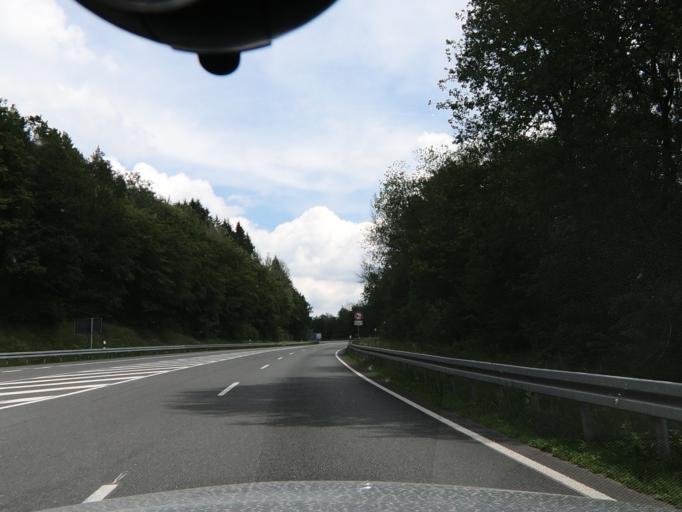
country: DE
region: North Rhine-Westphalia
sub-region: Regierungsbezirk Arnsberg
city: Meschede
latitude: 51.3854
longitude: 8.2966
